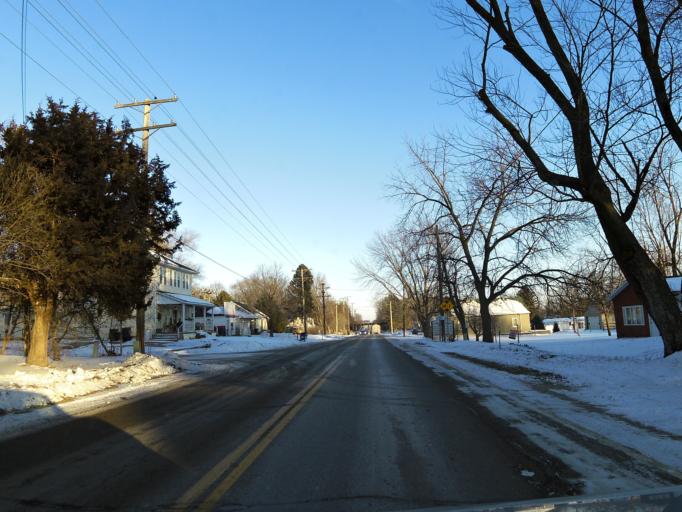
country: US
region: Minnesota
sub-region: Rice County
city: Northfield
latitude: 44.5437
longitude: -93.1552
